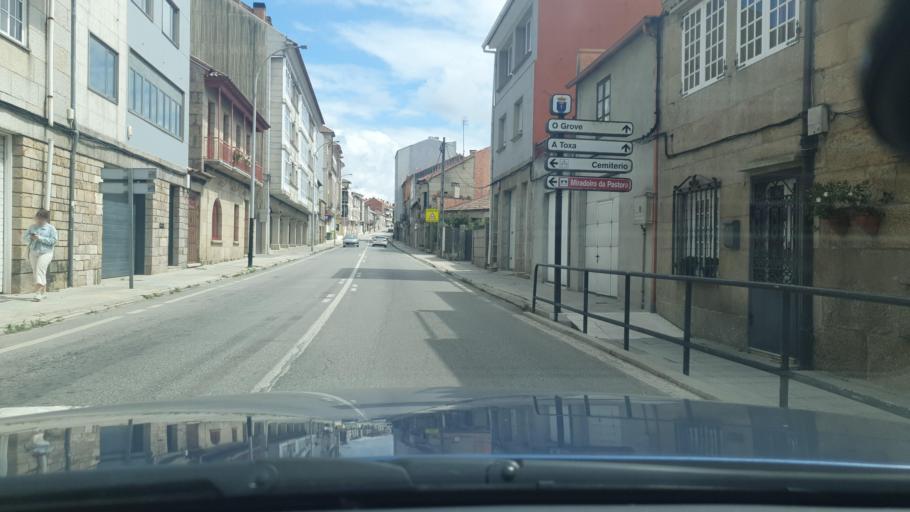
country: ES
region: Galicia
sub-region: Provincia de Pontevedra
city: Cambados
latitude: 42.5108
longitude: -8.8156
